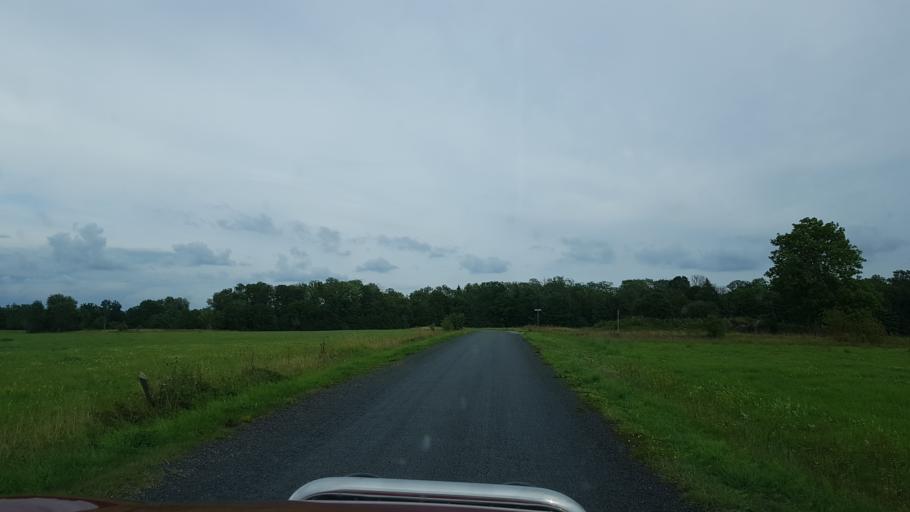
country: EE
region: Laeaene
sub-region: Ridala Parish
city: Uuemoisa
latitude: 58.9768
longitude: 23.7757
